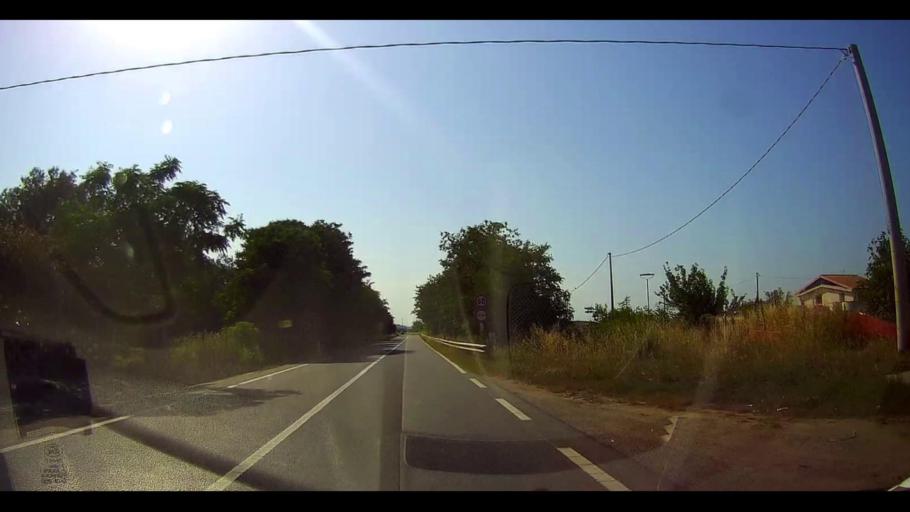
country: IT
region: Calabria
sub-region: Provincia di Crotone
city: Torretta
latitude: 39.4774
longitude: 17.0006
